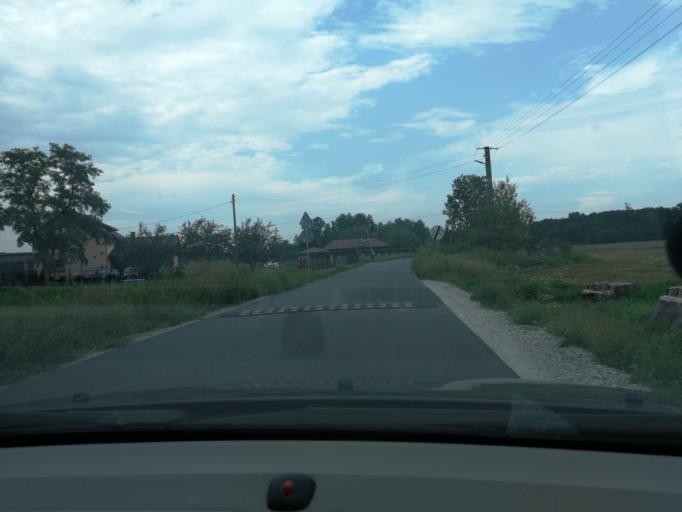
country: PL
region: Masovian Voivodeship
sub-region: Powiat warszawski zachodni
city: Bieniewice
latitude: 52.1069
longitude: 20.5549
